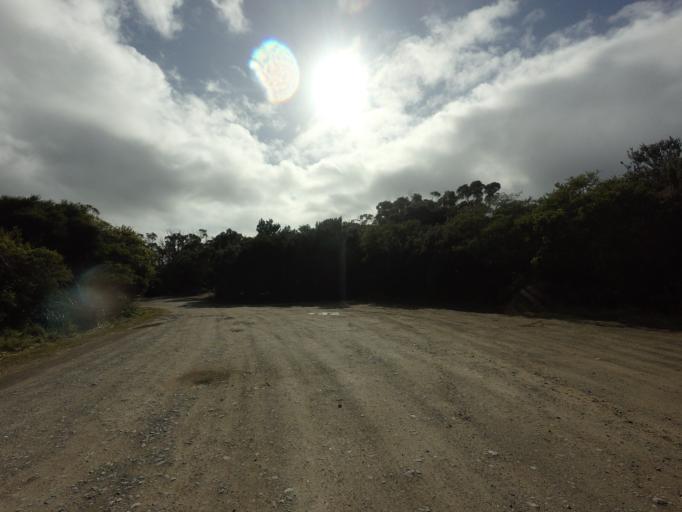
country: AU
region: Tasmania
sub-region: Huon Valley
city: Geeveston
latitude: -43.5789
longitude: 146.9009
